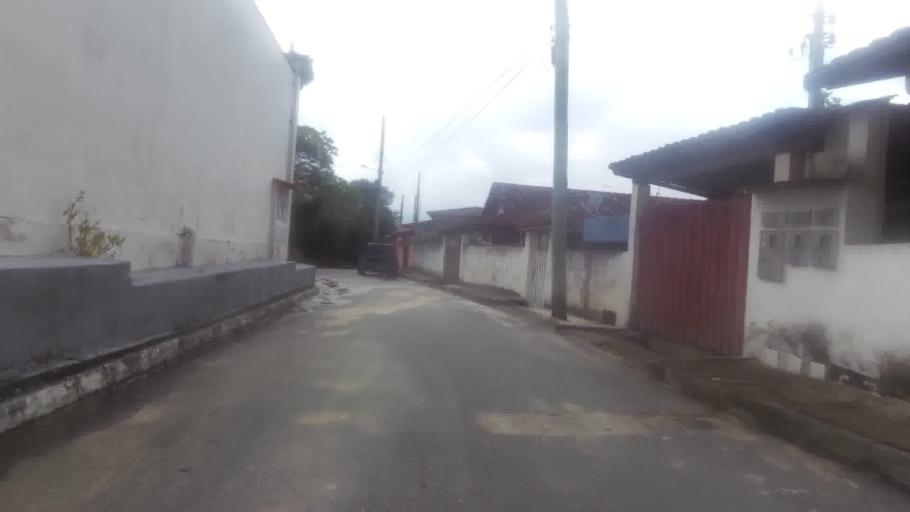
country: BR
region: Espirito Santo
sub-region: Guarapari
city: Guarapari
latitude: -20.7629
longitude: -40.5768
